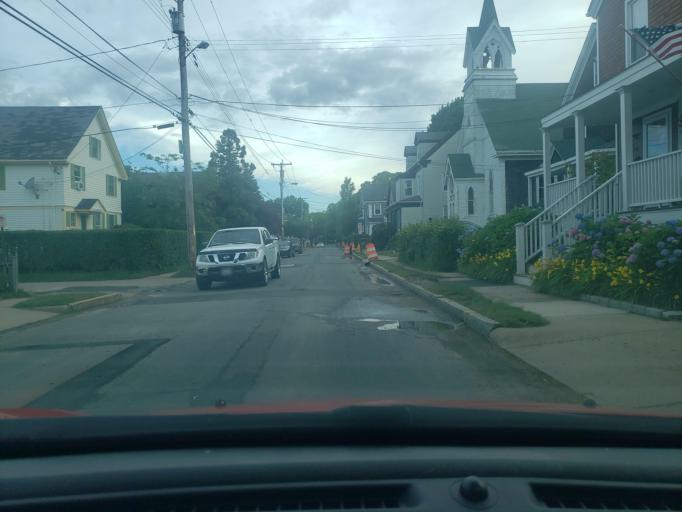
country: US
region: Rhode Island
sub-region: Newport County
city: Newport
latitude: 41.4818
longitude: -71.3023
